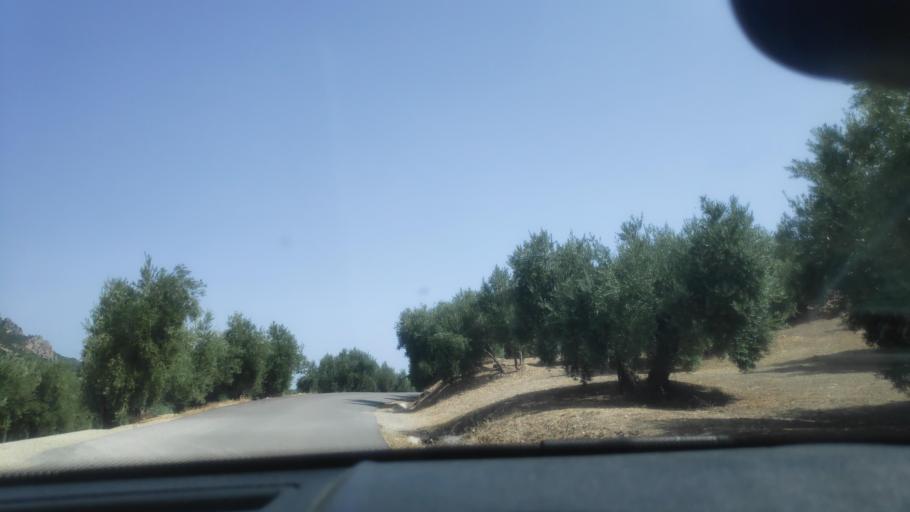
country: ES
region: Andalusia
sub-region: Provincia de Jaen
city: Torres
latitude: 37.7884
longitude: -3.4550
